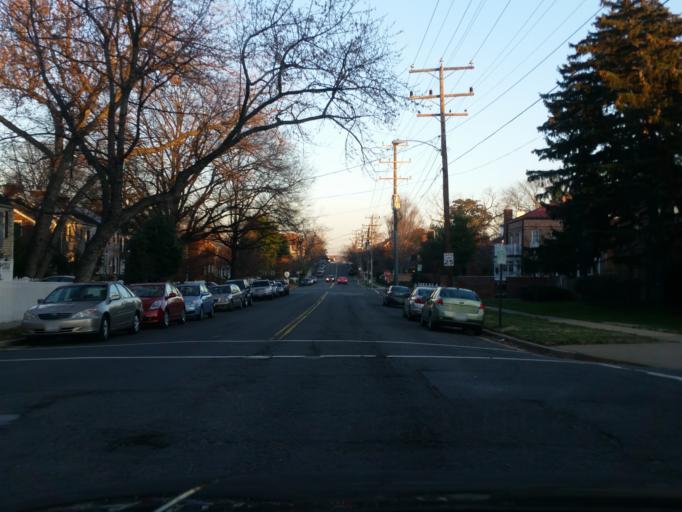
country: US
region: Virginia
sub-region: City of Alexandria
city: Alexandria
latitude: 38.7980
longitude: -77.0474
